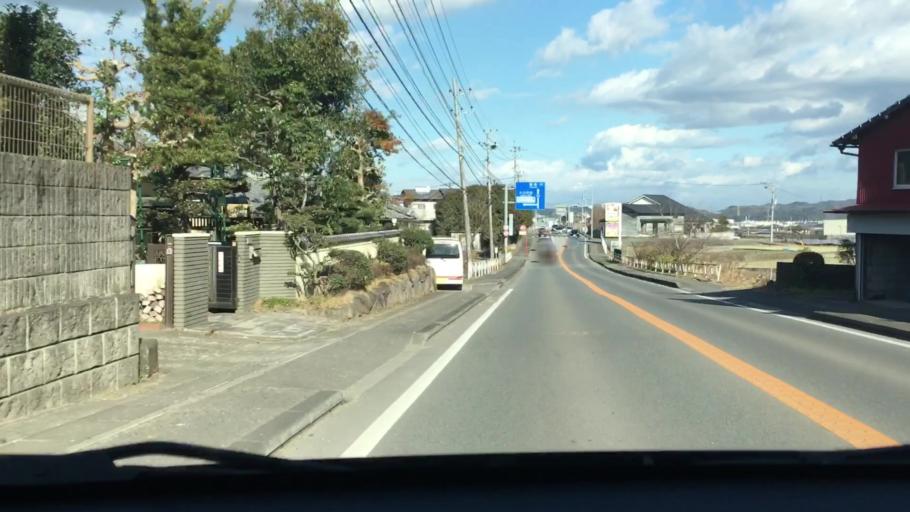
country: JP
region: Oita
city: Tsurusaki
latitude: 33.1754
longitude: 131.6596
